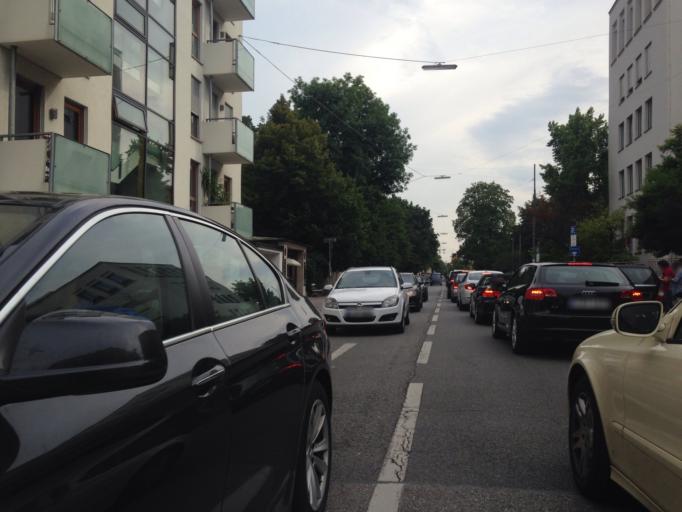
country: DE
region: Bavaria
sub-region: Upper Bavaria
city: Munich
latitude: 48.1483
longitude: 11.5654
